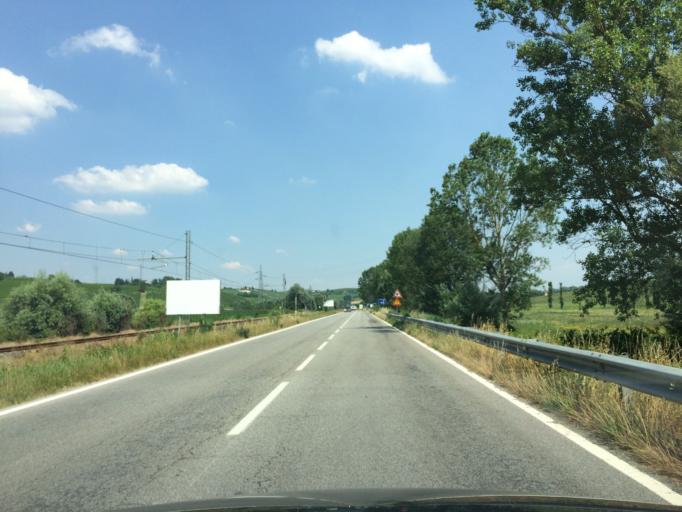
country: IT
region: Piedmont
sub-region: Provincia di Asti
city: Castelnuovo Calcea
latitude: 44.7766
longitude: 8.2853
